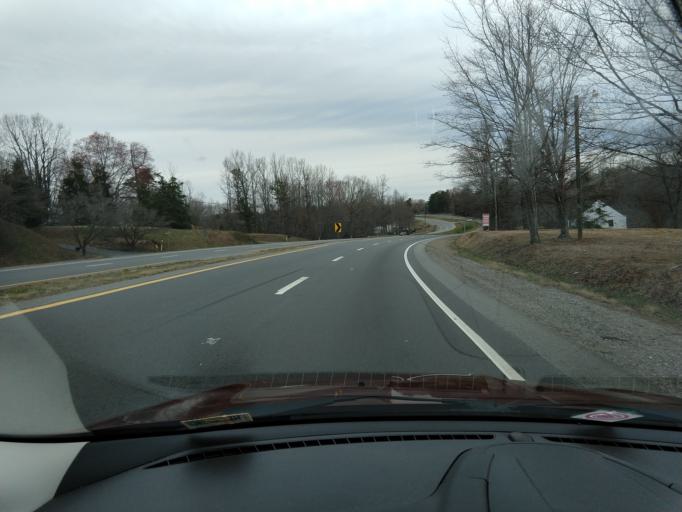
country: US
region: Virginia
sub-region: Henry County
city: Stanleytown
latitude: 36.7996
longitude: -79.9361
